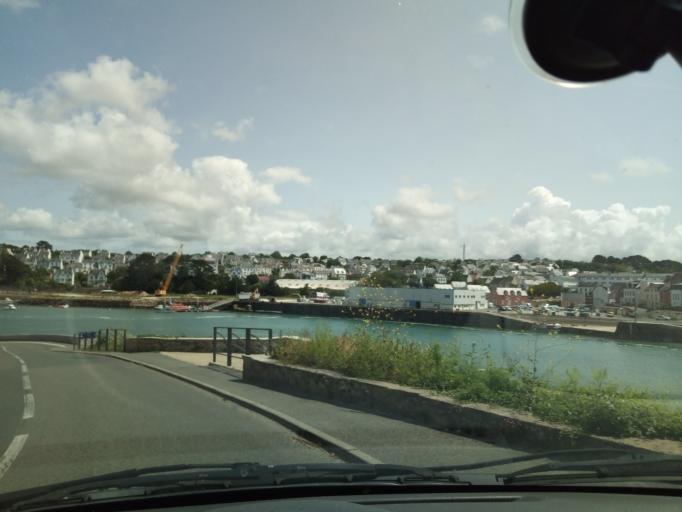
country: FR
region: Brittany
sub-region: Departement du Finistere
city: Audierne
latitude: 48.0182
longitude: -4.5356
